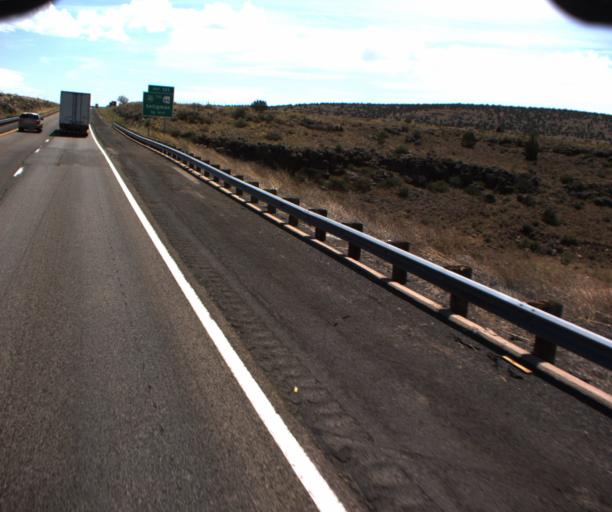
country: US
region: Arizona
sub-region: Mohave County
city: Peach Springs
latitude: 35.3219
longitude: -112.9069
